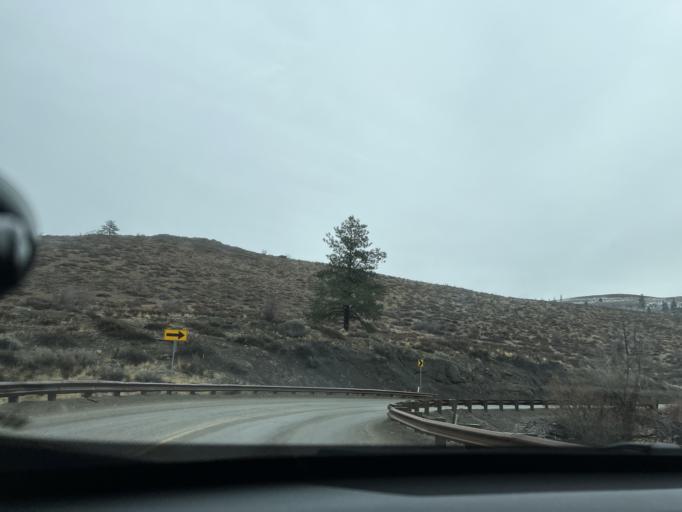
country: US
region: Washington
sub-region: Chelan County
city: Granite Falls
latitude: 48.4674
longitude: -120.2511
